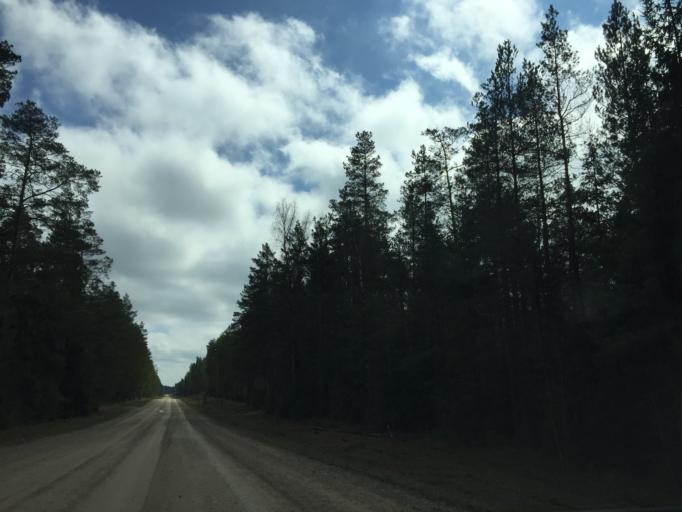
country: EE
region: Valgamaa
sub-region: Valga linn
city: Valga
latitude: 57.6610
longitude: 26.2019
